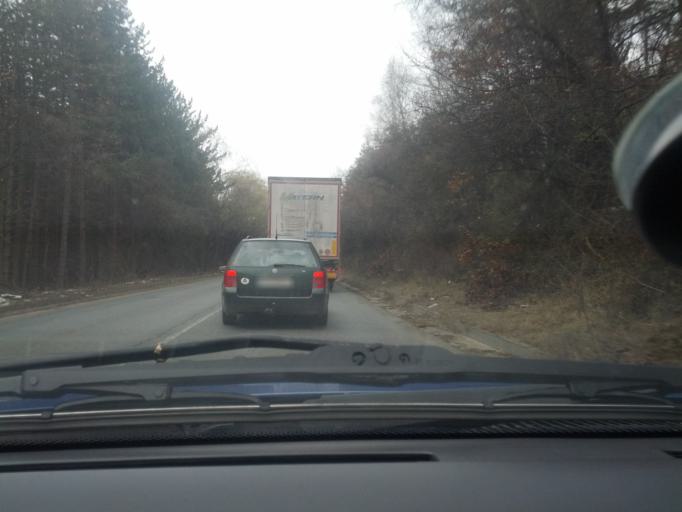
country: BG
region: Vratsa
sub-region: Obshtina Mezdra
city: Mezdra
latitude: 43.0127
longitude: 23.6942
